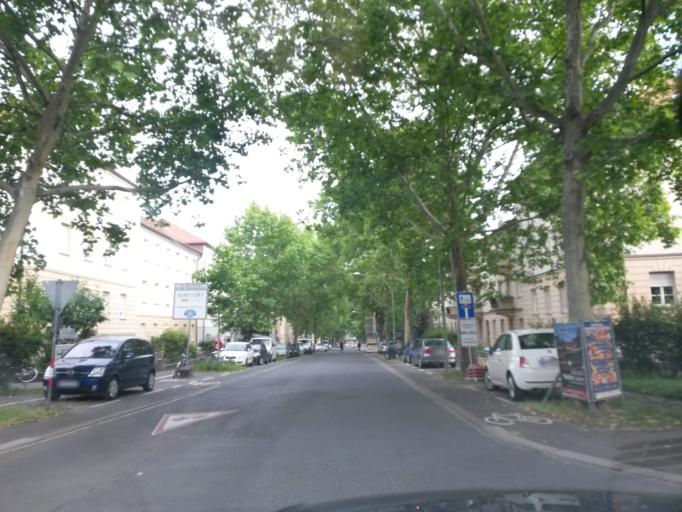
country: DE
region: Bavaria
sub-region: Regierungsbezirk Unterfranken
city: Wuerzburg
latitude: 49.7872
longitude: 9.9510
